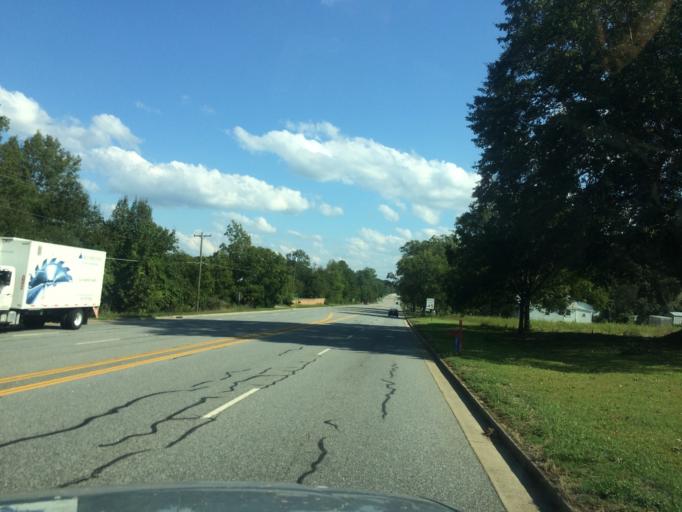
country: US
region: South Carolina
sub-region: Greenwood County
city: Ware Shoals
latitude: 34.4399
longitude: -82.2502
